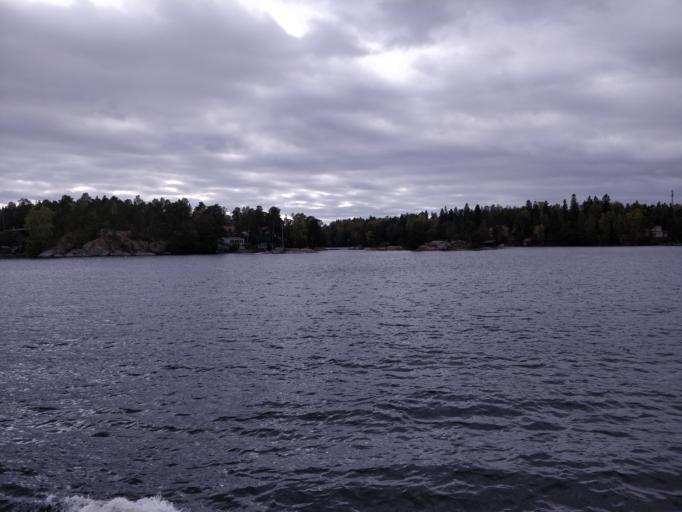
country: FI
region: Uusimaa
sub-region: Helsinki
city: Vantaa
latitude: 60.1711
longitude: 25.0933
